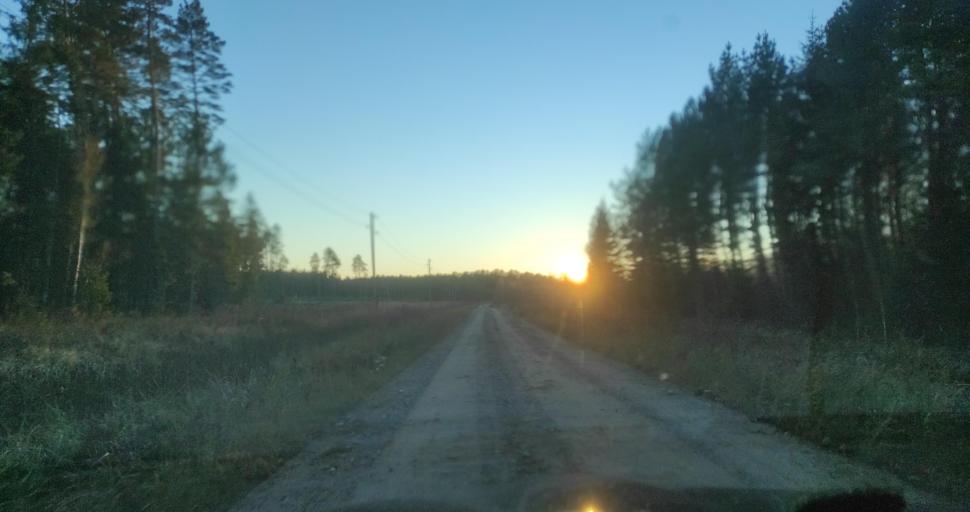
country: LV
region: Dundaga
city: Dundaga
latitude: 57.3696
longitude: 22.0720
